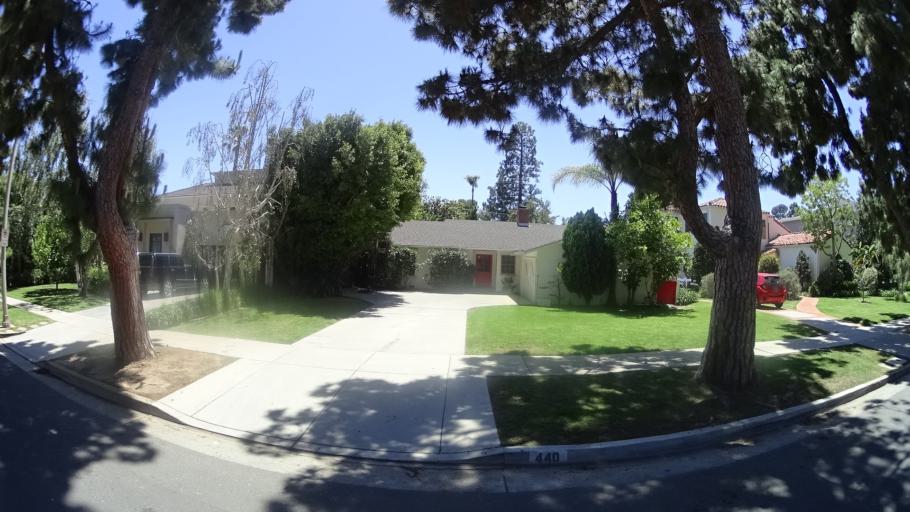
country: US
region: California
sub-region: Los Angeles County
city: Santa Monica
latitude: 34.0437
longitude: -118.4897
